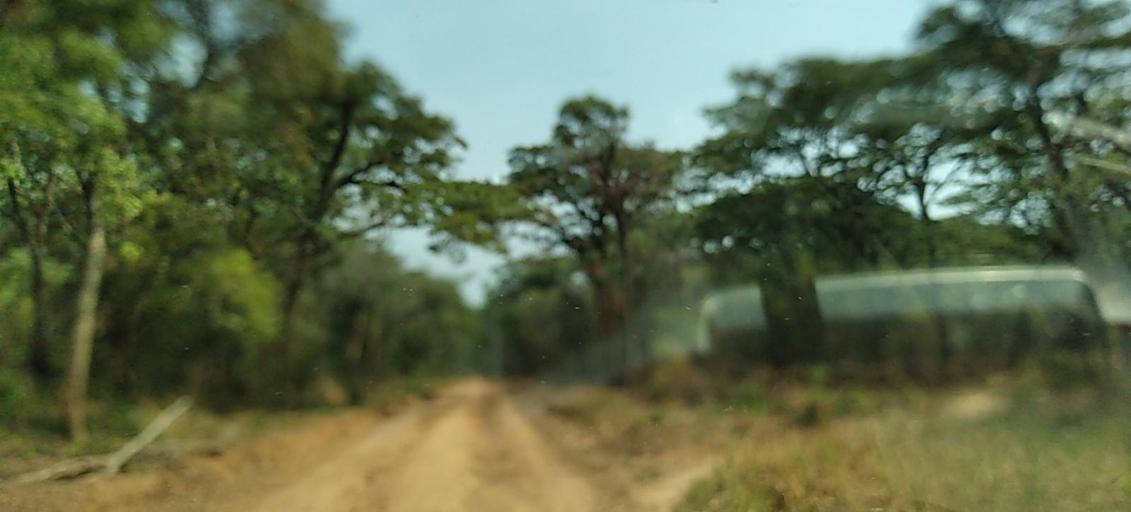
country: ZM
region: North-Western
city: Kansanshi
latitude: -12.0600
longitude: 26.8884
